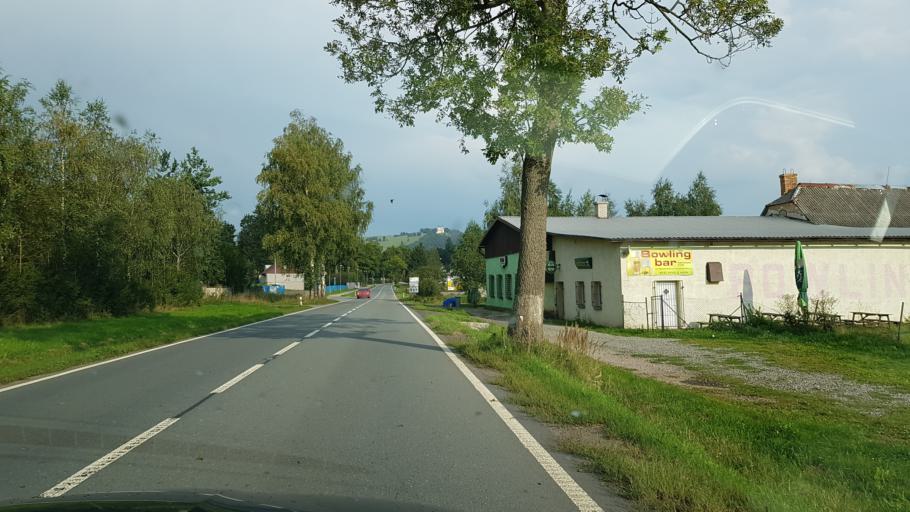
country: CZ
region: Pardubicky
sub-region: Okres Usti nad Orlici
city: Kraliky
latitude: 50.0847
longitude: 16.7425
